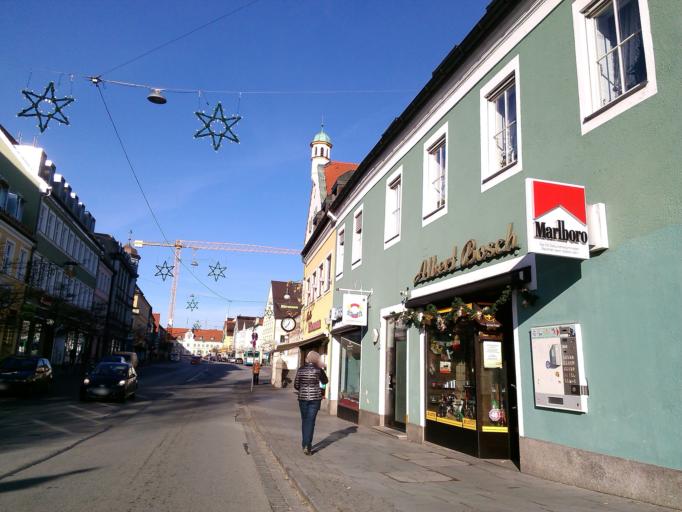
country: DE
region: Bavaria
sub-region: Upper Bavaria
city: Fuerstenfeldbruck
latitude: 48.1769
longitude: 11.2557
